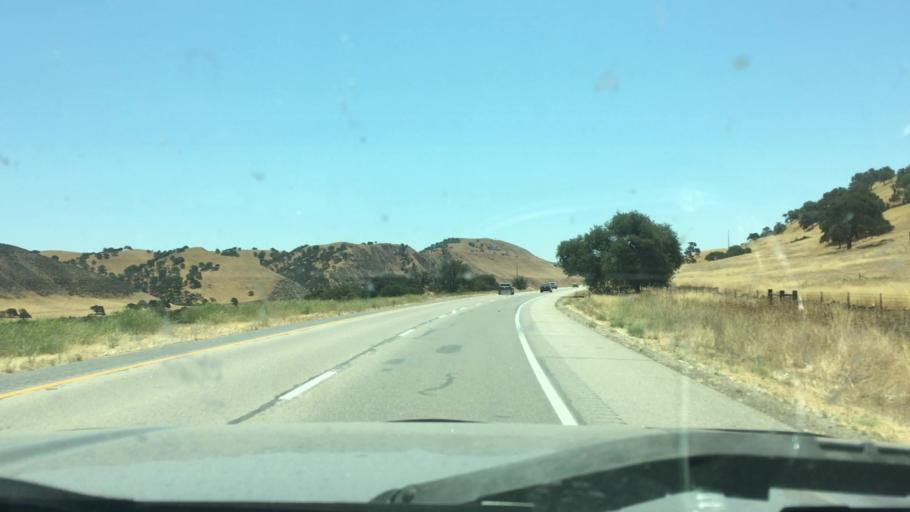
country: US
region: California
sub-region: San Luis Obispo County
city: Lake Nacimiento
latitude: 35.9098
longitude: -120.8480
